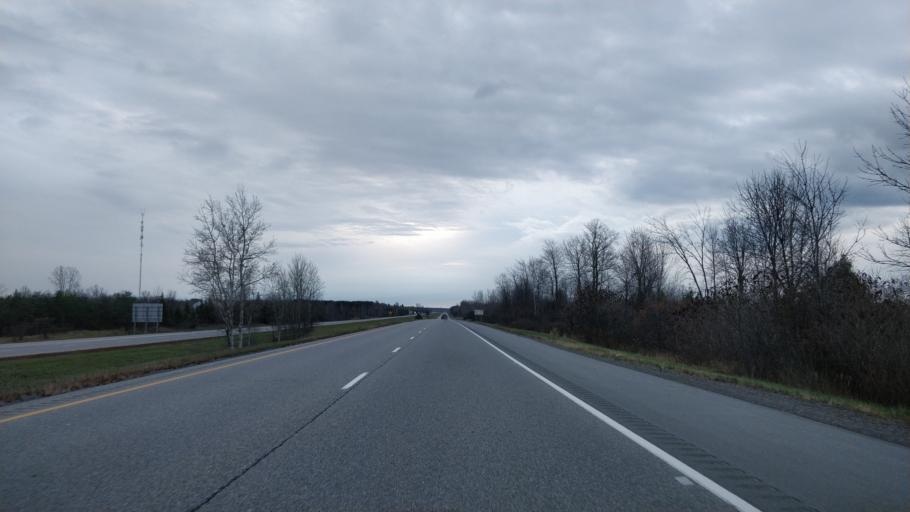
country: CA
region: Ontario
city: Prescott
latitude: 44.9775
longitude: -75.6083
